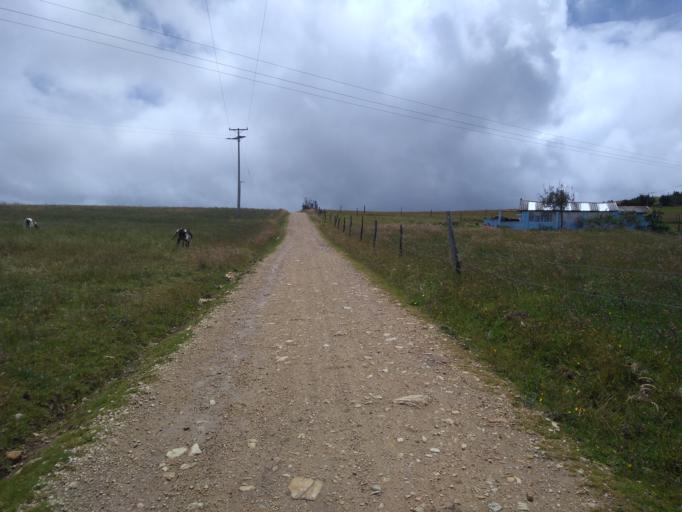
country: CO
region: Boyaca
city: Toca
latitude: 5.5891
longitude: -73.1382
